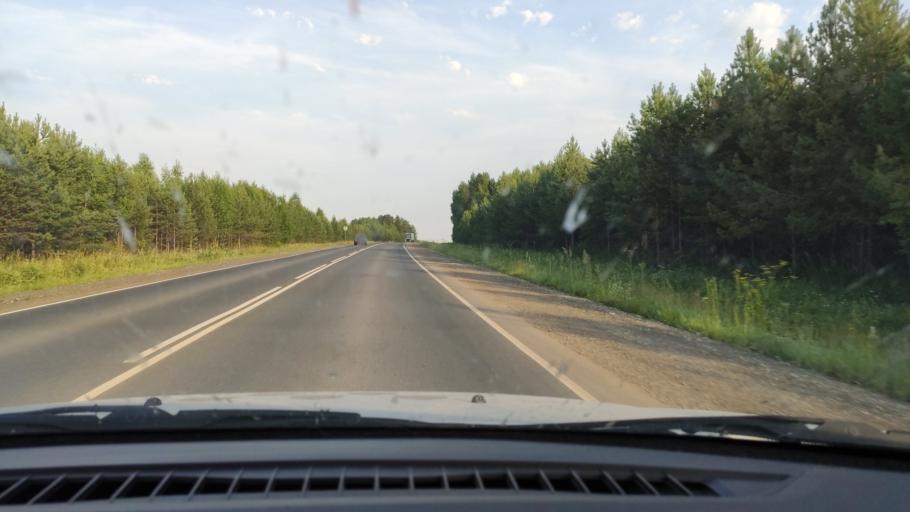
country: RU
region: Perm
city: Siva
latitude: 58.4289
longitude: 54.4475
